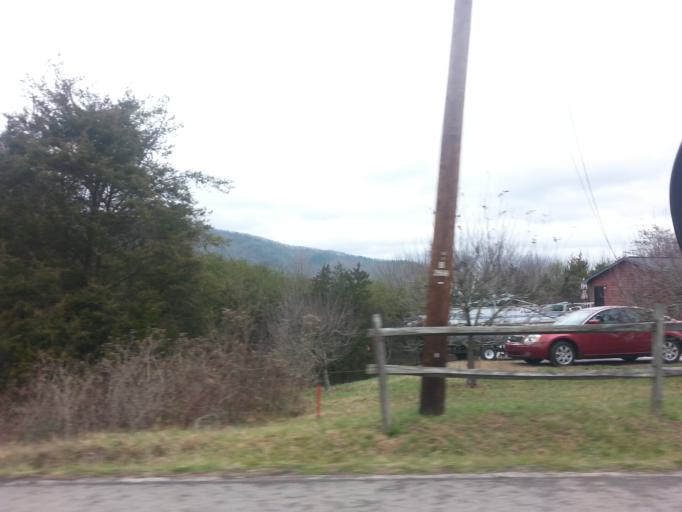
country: US
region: Tennessee
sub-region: Grainger County
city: Blaine
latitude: 36.1528
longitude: -83.7228
